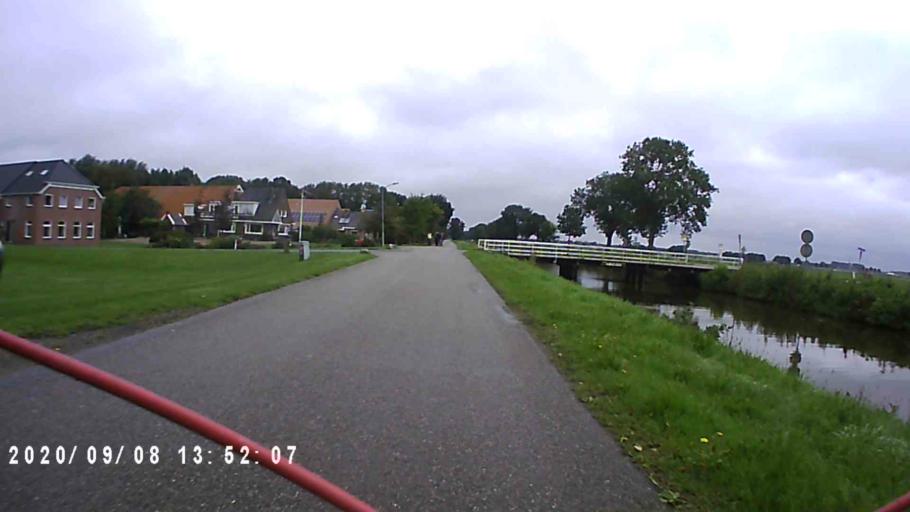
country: NL
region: Groningen
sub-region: Gemeente Veendam
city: Veendam
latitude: 53.1441
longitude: 6.8666
